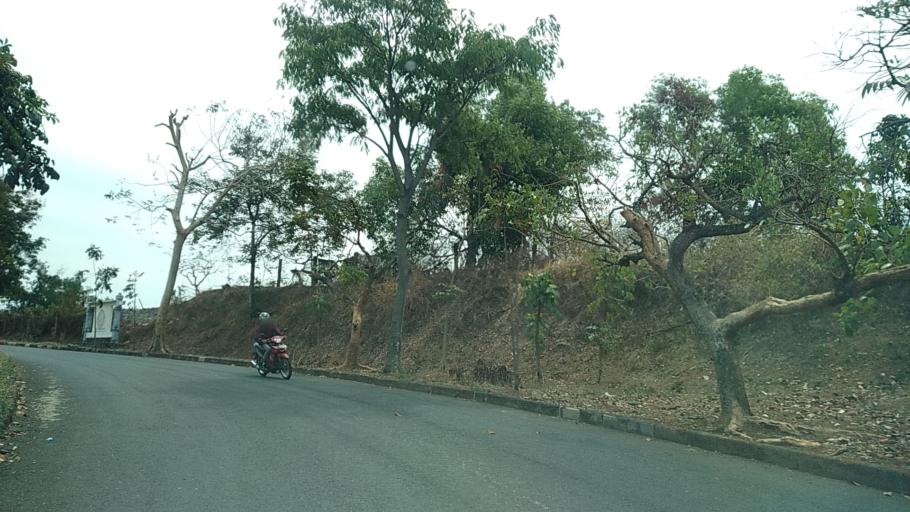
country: ID
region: Central Java
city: Semarang
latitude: -7.0471
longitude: 110.4354
